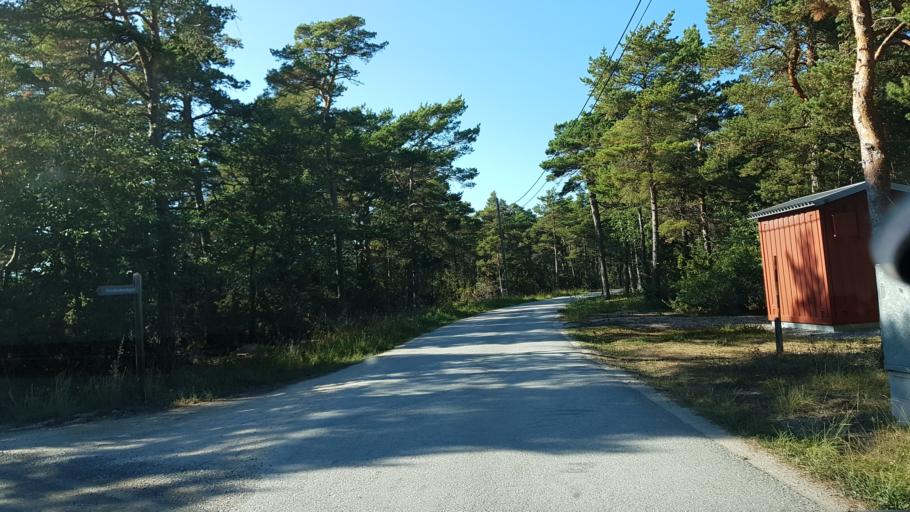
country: SE
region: Gotland
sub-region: Gotland
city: Visby
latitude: 57.7911
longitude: 18.4455
